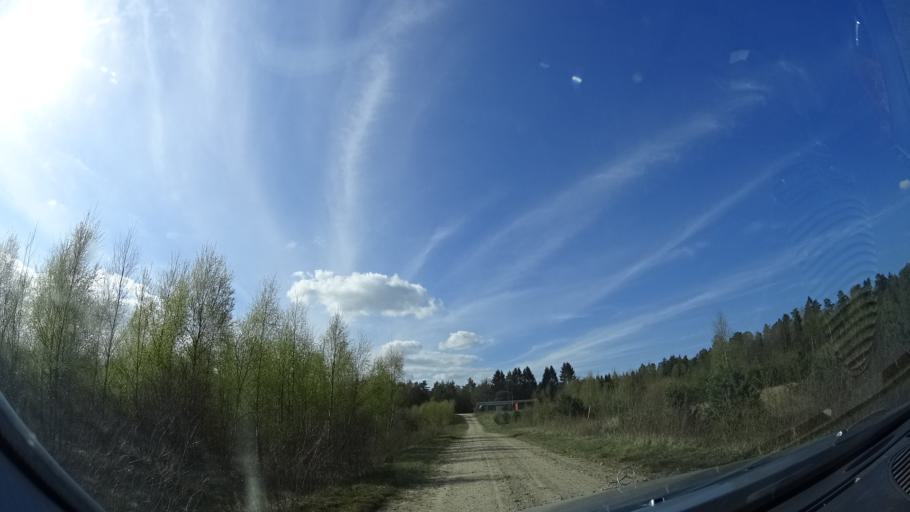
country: SE
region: Skane
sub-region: Hassleholms Kommun
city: Tormestorp
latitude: 56.1054
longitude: 13.6800
